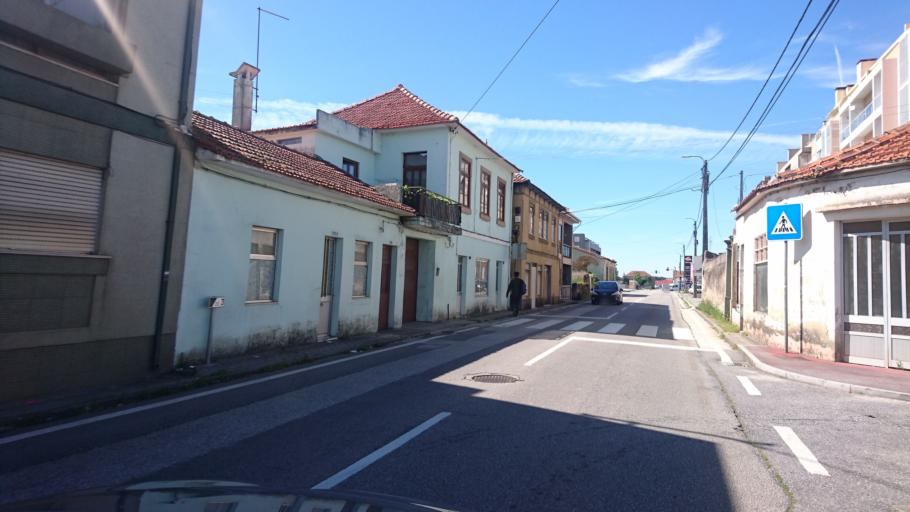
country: PT
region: Aveiro
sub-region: Ovar
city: Esmoriz
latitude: 40.9617
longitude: -8.6281
